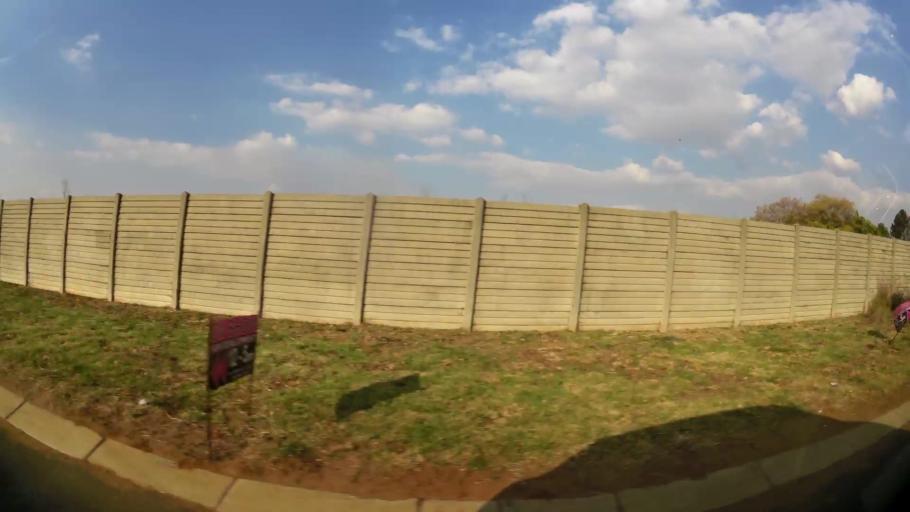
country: ZA
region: Gauteng
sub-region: Ekurhuleni Metropolitan Municipality
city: Benoni
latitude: -26.1101
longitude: 28.2808
